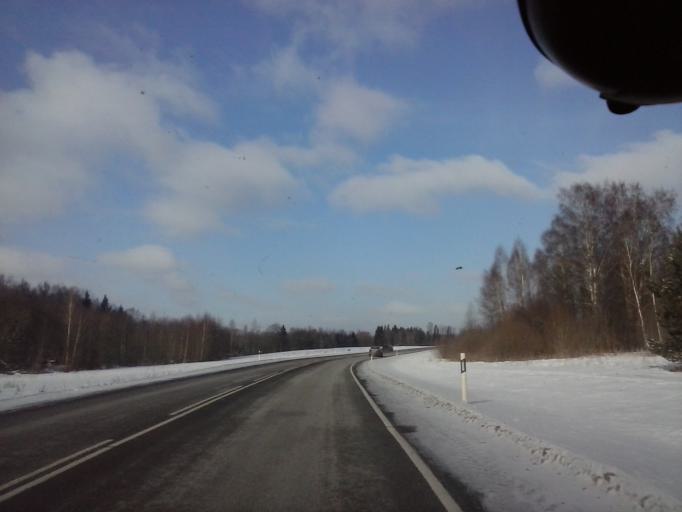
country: EE
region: Viljandimaa
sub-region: Viljandi linn
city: Viljandi
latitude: 58.3432
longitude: 25.4662
